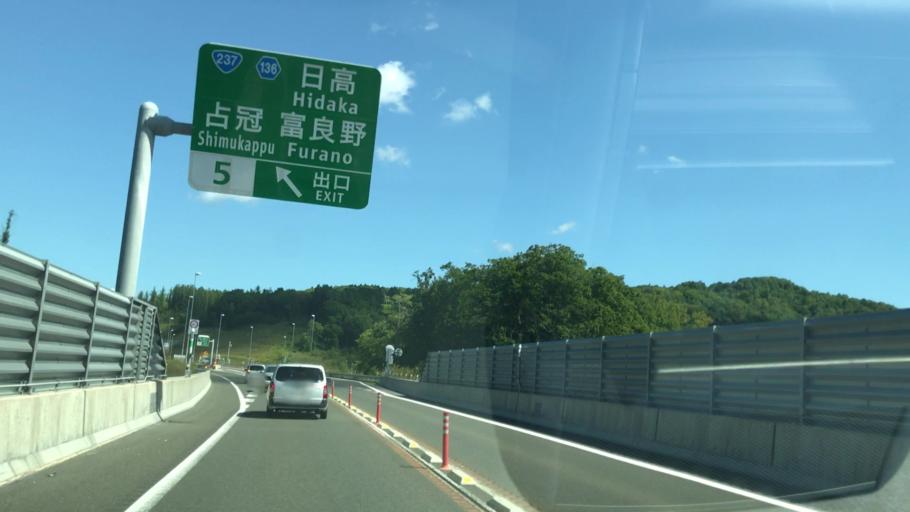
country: JP
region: Hokkaido
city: Shimo-furano
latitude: 42.9771
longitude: 142.4066
